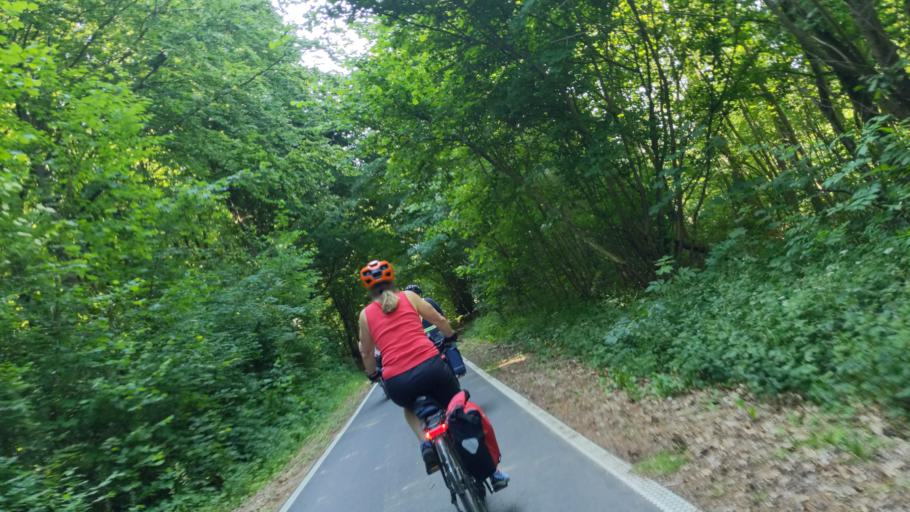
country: DE
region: Schleswig-Holstein
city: Krummesse
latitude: 53.7912
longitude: 10.6307
